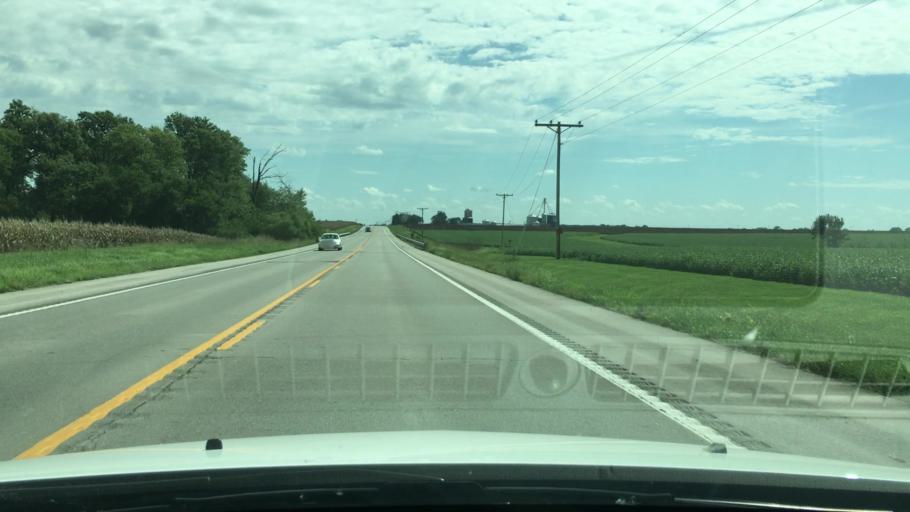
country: US
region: Missouri
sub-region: Audrain County
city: Mexico
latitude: 39.1638
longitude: -91.7512
